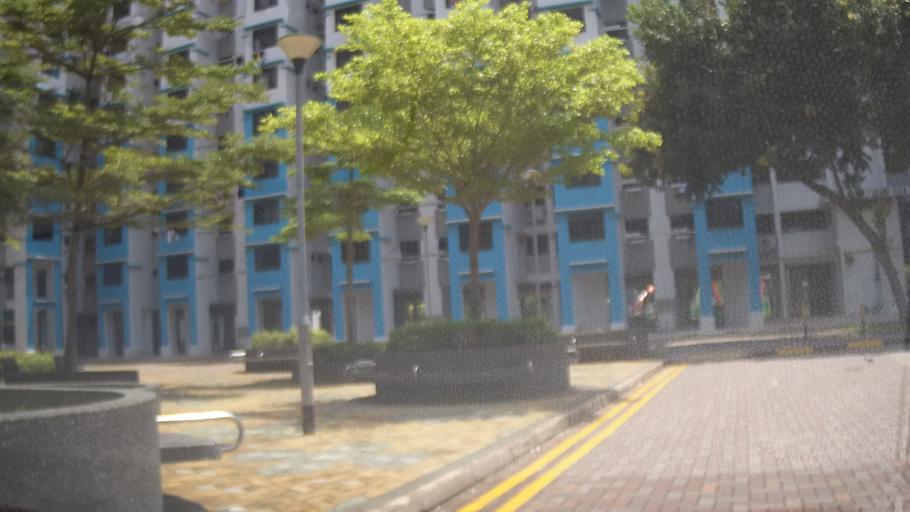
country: SG
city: Singapore
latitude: 1.3216
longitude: 103.8685
